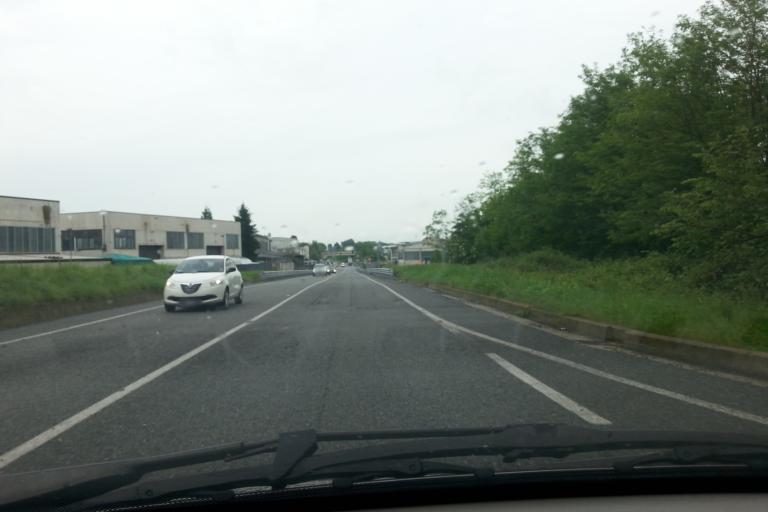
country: IT
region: Piedmont
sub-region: Provincia di Torino
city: Alpignano
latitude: 45.1094
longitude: 7.5068
